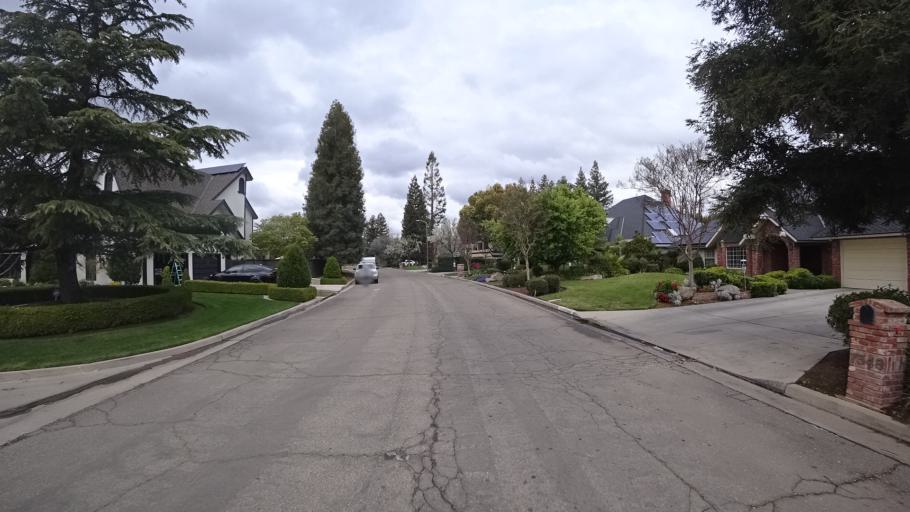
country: US
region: California
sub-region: Fresno County
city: Fresno
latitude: 36.8469
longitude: -119.8429
